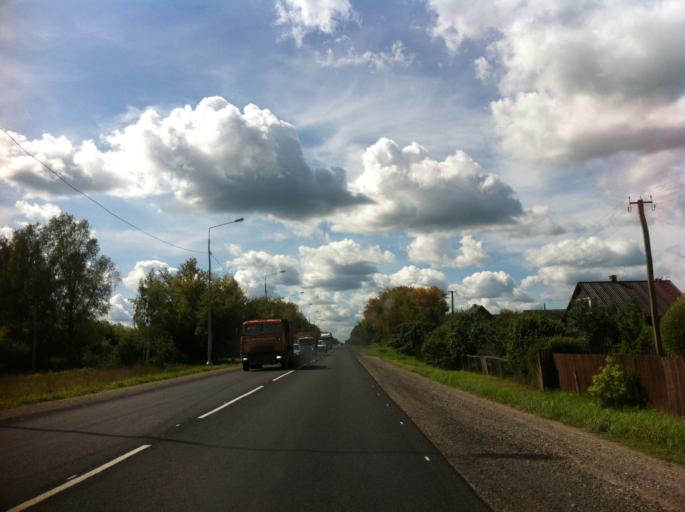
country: RU
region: Pskov
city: Izborsk
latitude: 57.7307
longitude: 27.9732
